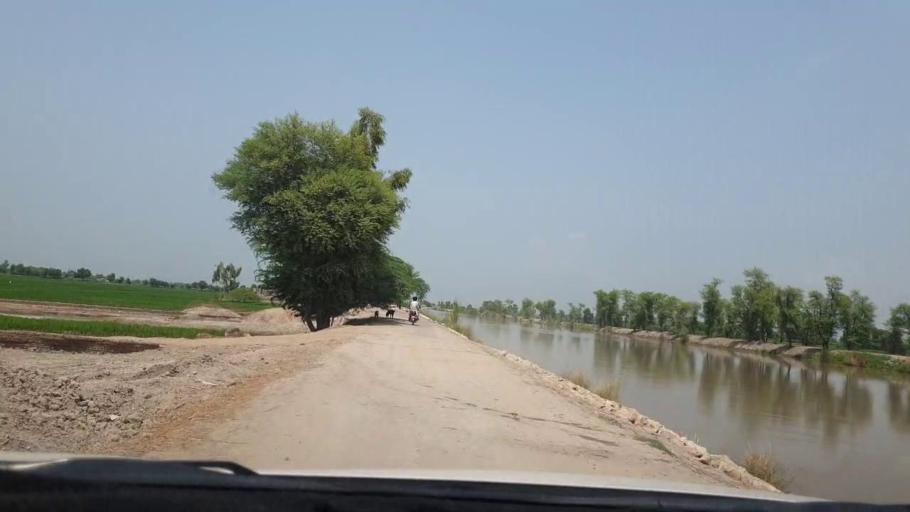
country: PK
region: Sindh
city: Dokri
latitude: 27.3281
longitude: 68.1091
